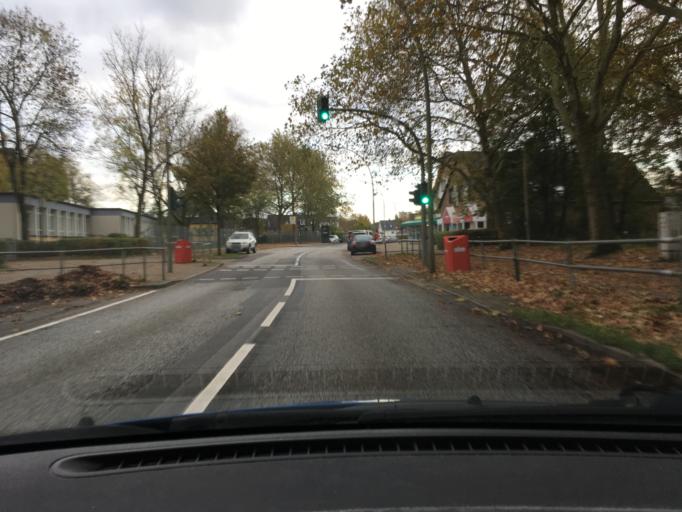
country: DE
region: Hamburg
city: Kleiner Grasbrook
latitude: 53.4939
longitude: 10.0125
